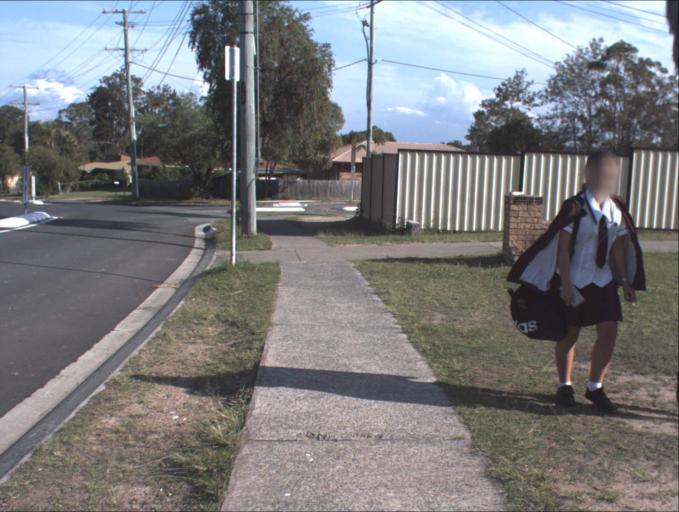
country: AU
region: Queensland
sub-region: Logan
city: Woodridge
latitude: -27.6687
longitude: 153.0556
